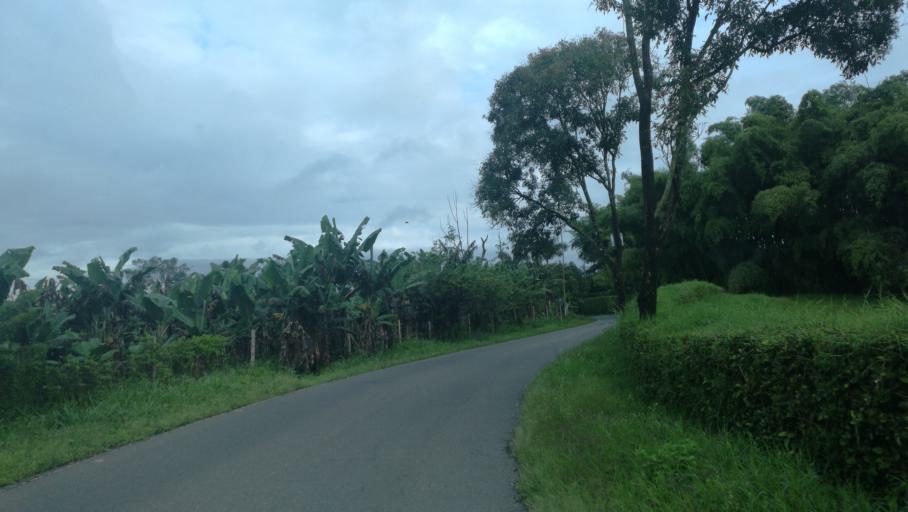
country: CO
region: Quindio
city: Montenegro
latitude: 4.5336
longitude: -75.7747
